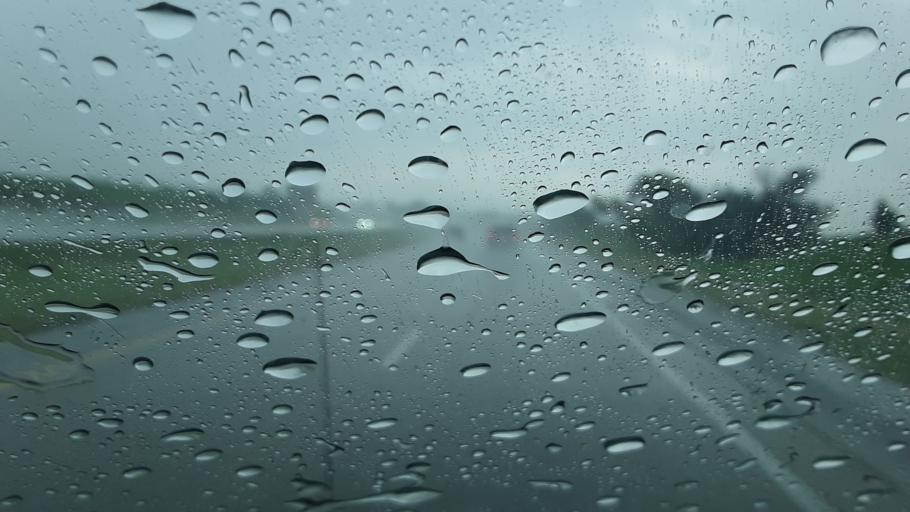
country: US
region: Iowa
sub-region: Pottawattamie County
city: Council Bluffs
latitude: 41.2713
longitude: -95.7910
